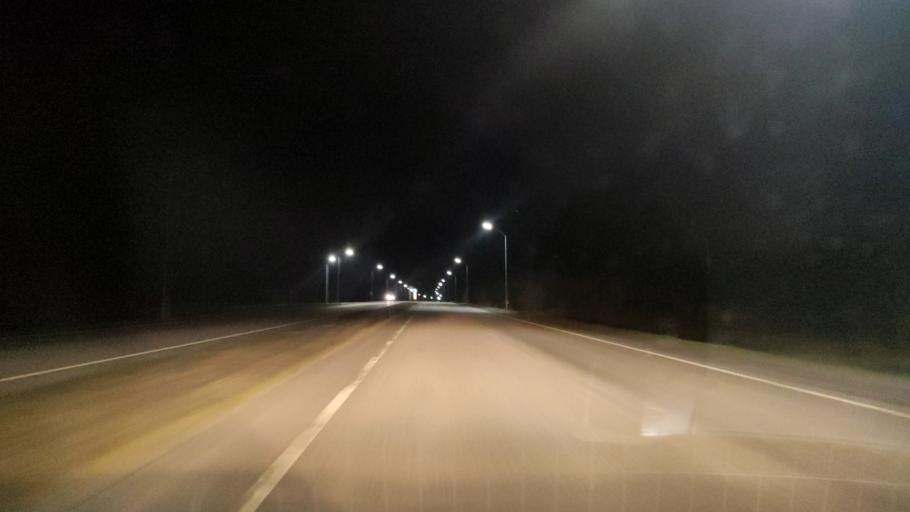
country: RU
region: Belgorod
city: Staryy Oskol
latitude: 51.3739
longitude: 37.8484
